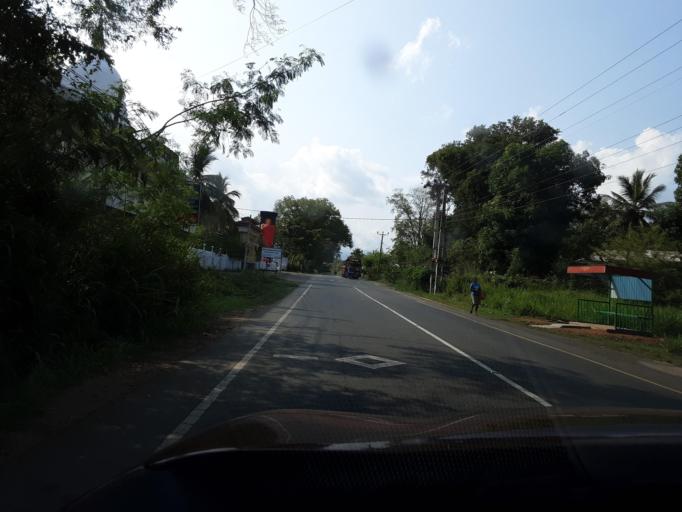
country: LK
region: Uva
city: Haputale
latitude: 6.6004
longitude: 81.1397
